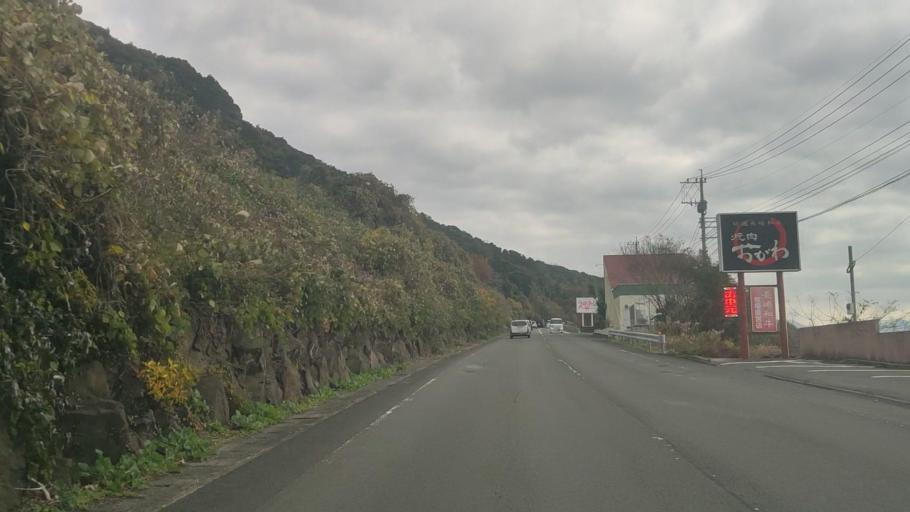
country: JP
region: Nagasaki
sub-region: Isahaya-shi
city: Isahaya
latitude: 32.7951
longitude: 130.1014
